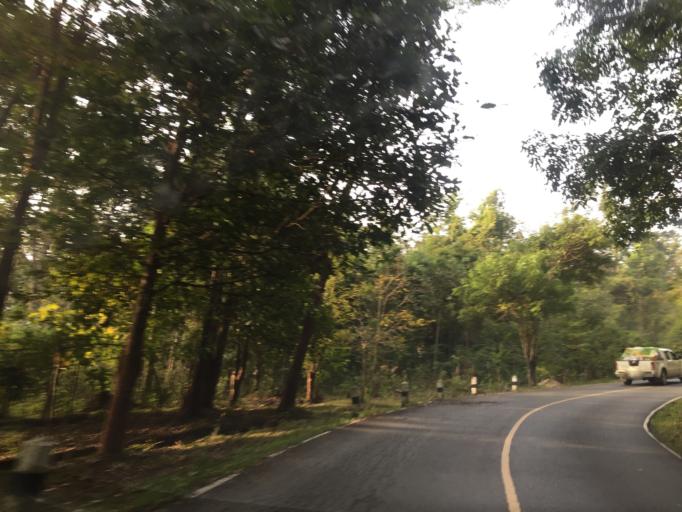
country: TH
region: Chiang Mai
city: Samoeng
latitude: 18.9594
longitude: 98.8358
